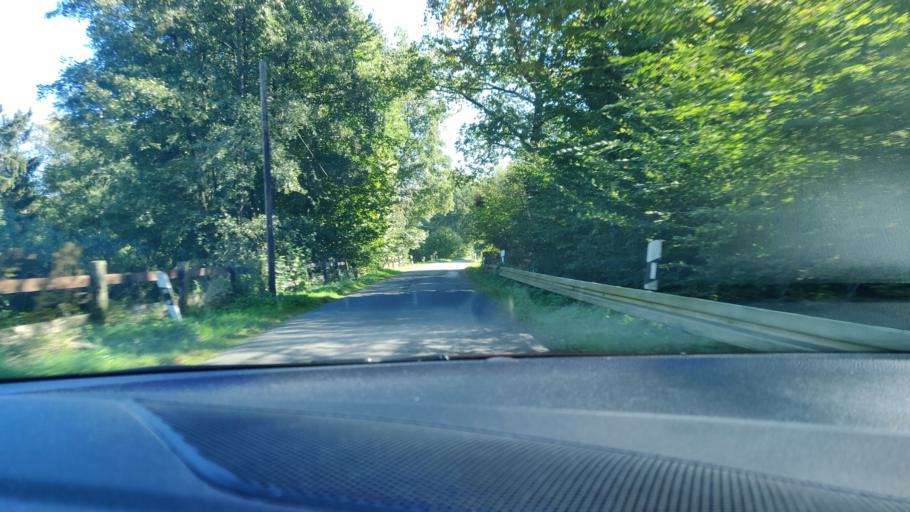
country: DE
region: North Rhine-Westphalia
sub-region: Regierungsbezirk Dusseldorf
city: Velbert
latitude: 51.3568
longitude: 7.0665
